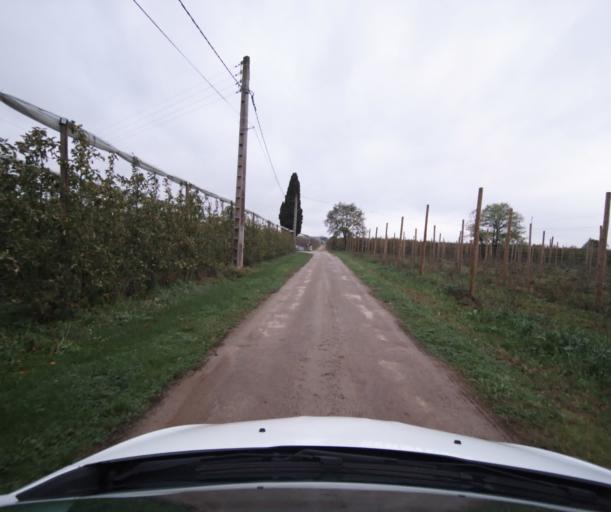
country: FR
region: Midi-Pyrenees
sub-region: Departement du Tarn-et-Garonne
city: Moissac
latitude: 44.0804
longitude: 1.1268
